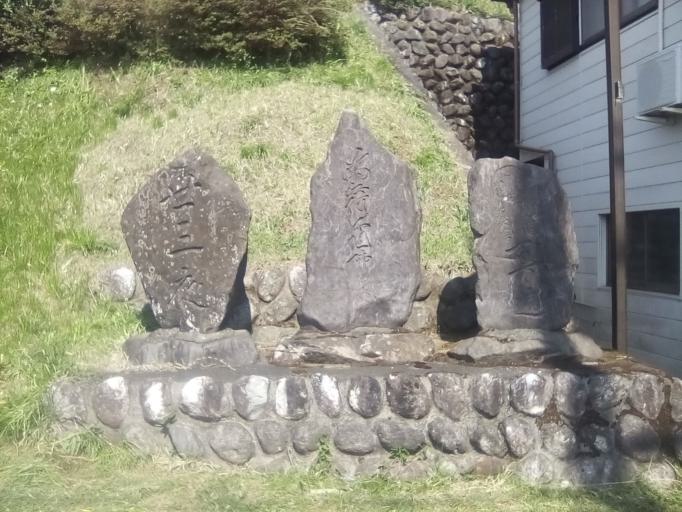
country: JP
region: Yamanashi
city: Uenohara
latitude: 35.5840
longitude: 139.1508
